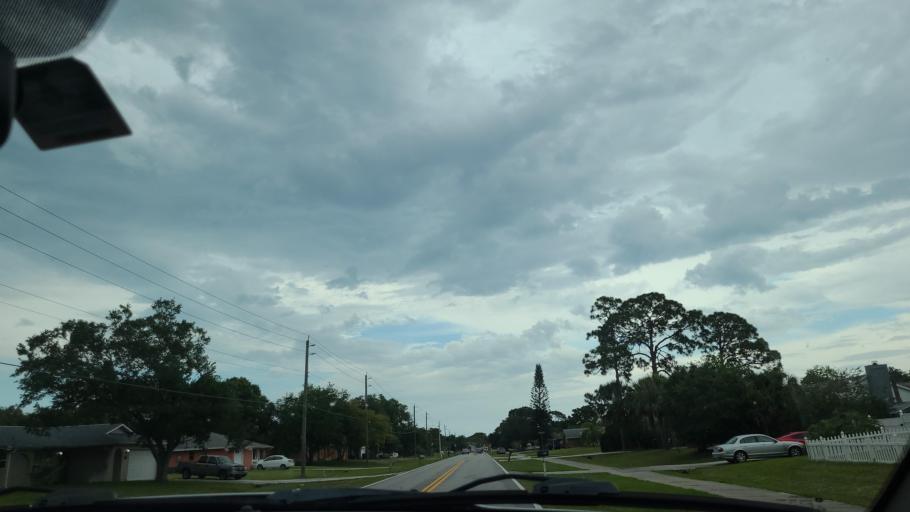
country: US
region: Florida
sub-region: Brevard County
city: West Melbourne
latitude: 28.0176
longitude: -80.6536
